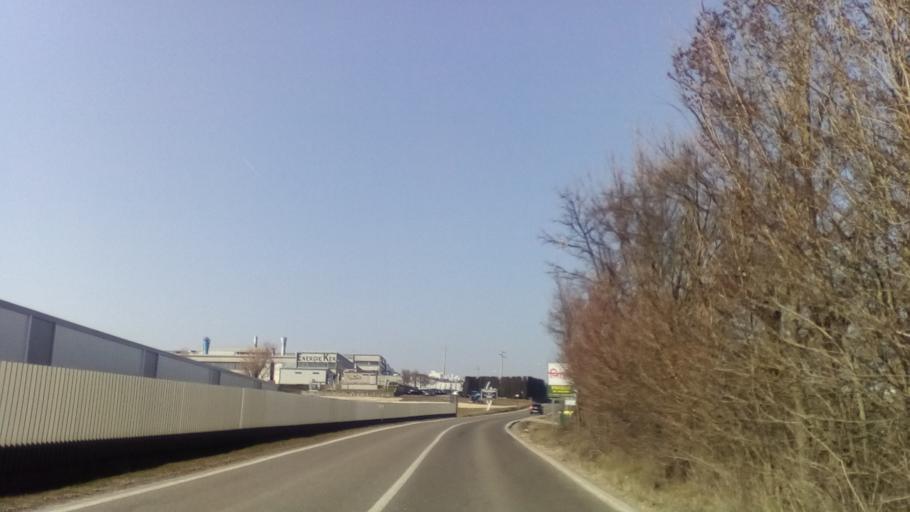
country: IT
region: Emilia-Romagna
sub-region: Provincia di Modena
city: Sant'Antonio
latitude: 44.3768
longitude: 10.8255
